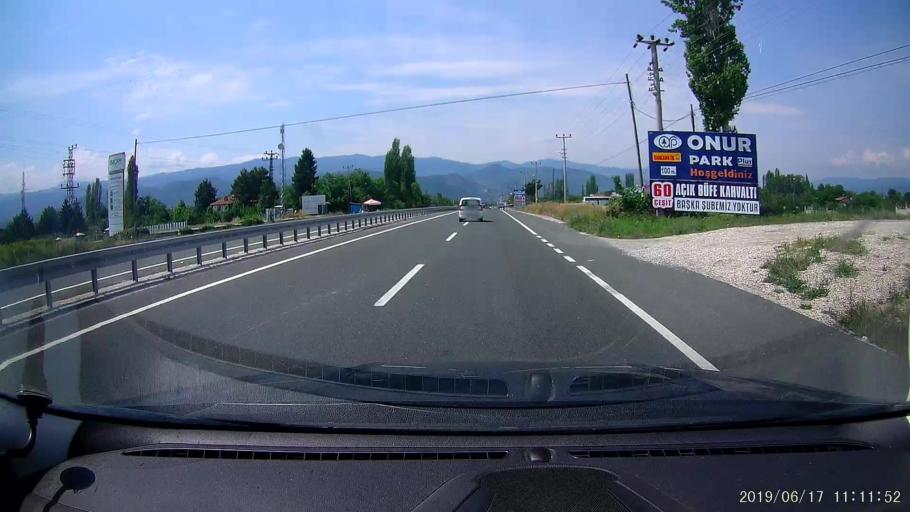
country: TR
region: Kastamonu
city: Tosya
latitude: 40.9806
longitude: 34.0037
